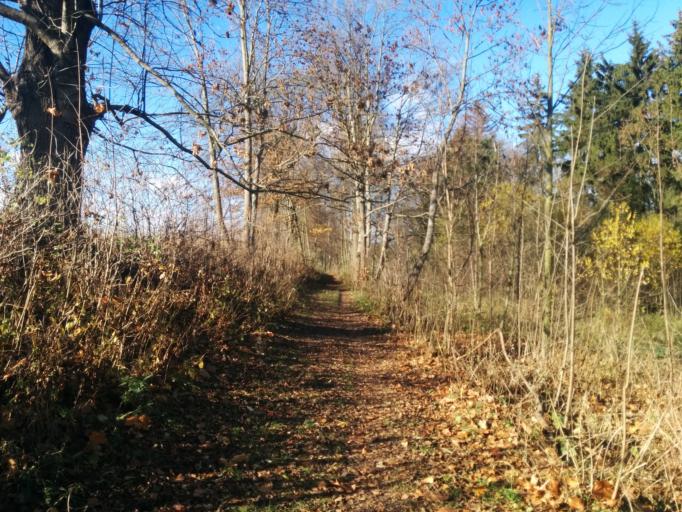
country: CZ
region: Vysocina
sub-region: Okres Jihlava
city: Jihlava
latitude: 49.4093
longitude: 15.5576
